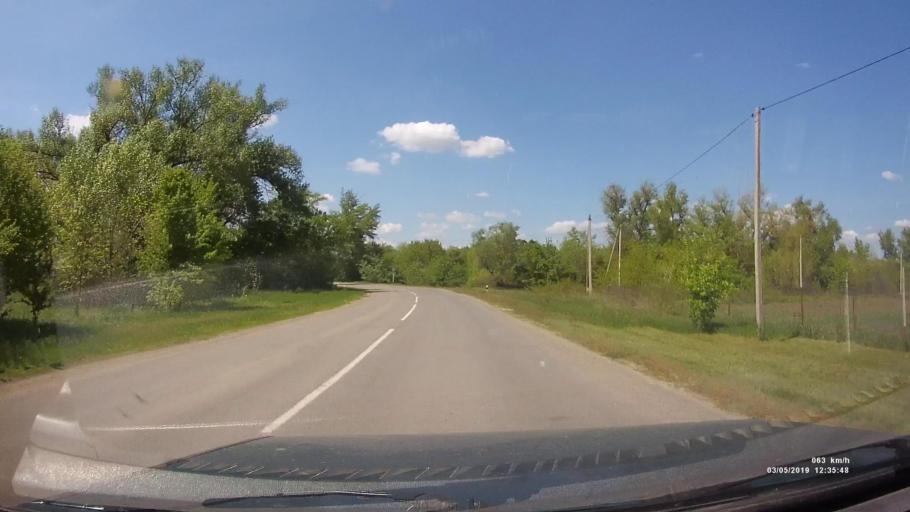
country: RU
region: Rostov
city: Semikarakorsk
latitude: 47.5290
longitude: 40.7572
